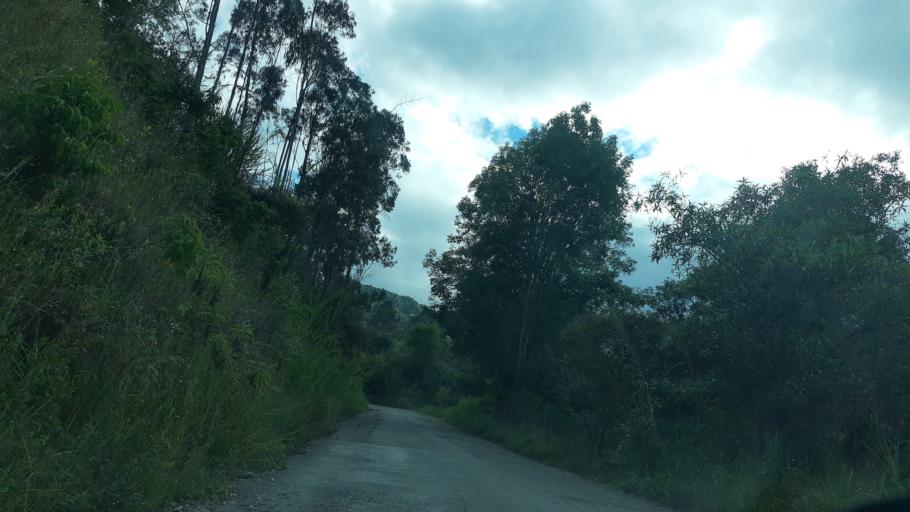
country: CO
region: Cundinamarca
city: Tenza
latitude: 5.0436
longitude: -73.4207
